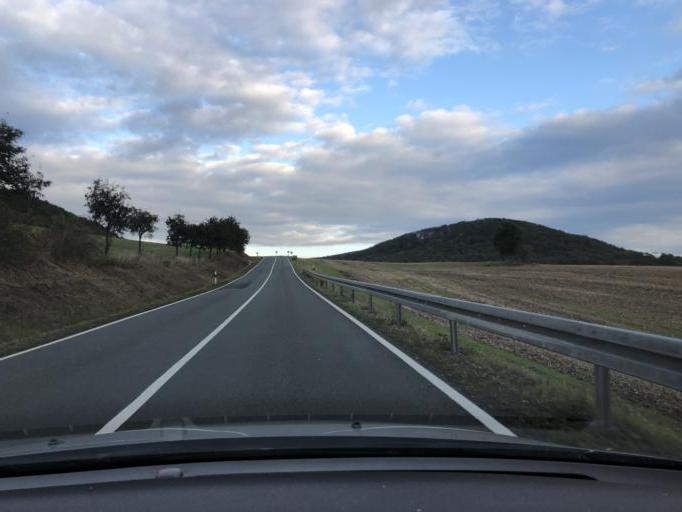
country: DE
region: Thuringia
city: Effelder
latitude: 51.2091
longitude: 10.2404
